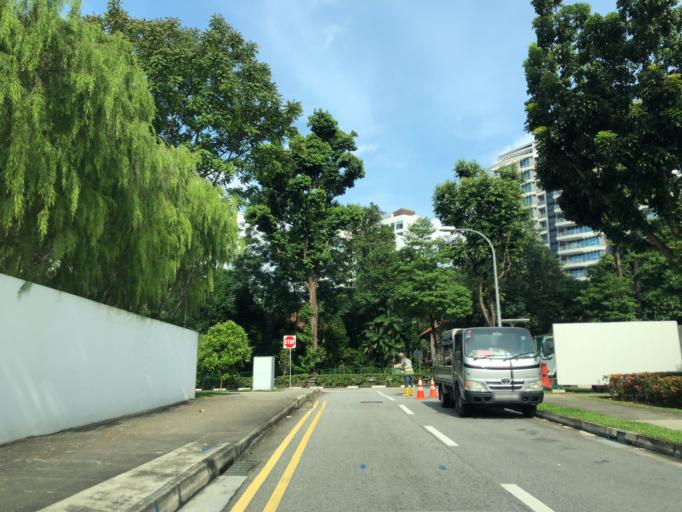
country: SG
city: Singapore
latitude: 1.3153
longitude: 103.8257
